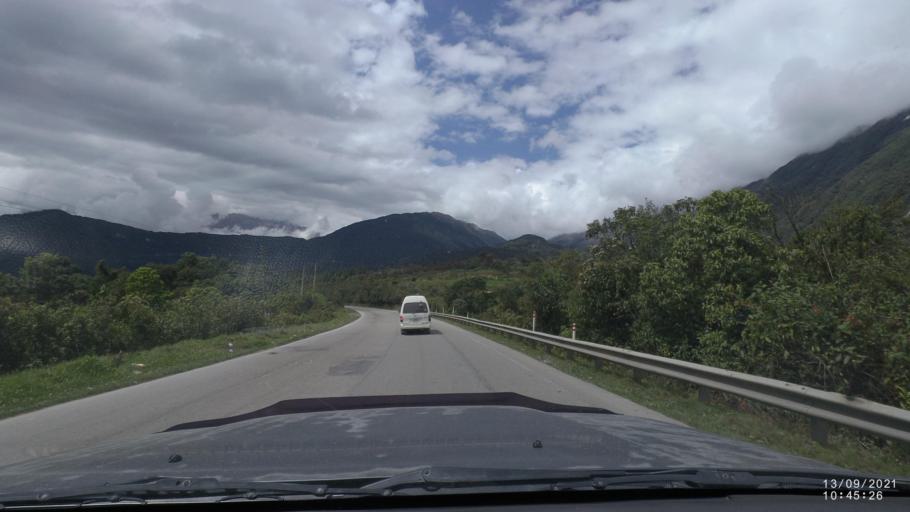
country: BO
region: Cochabamba
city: Colomi
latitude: -17.2022
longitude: -65.8760
